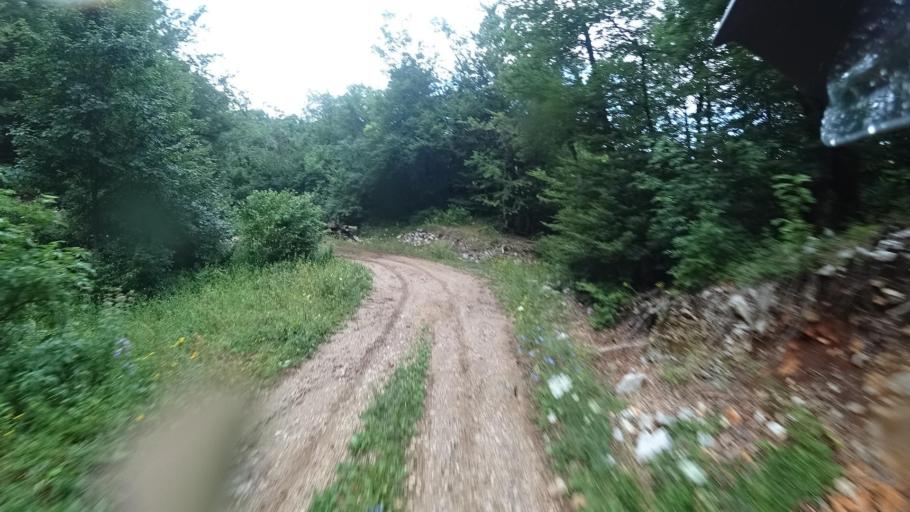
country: HR
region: Licko-Senjska
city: Jezerce
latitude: 44.7334
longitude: 15.6399
